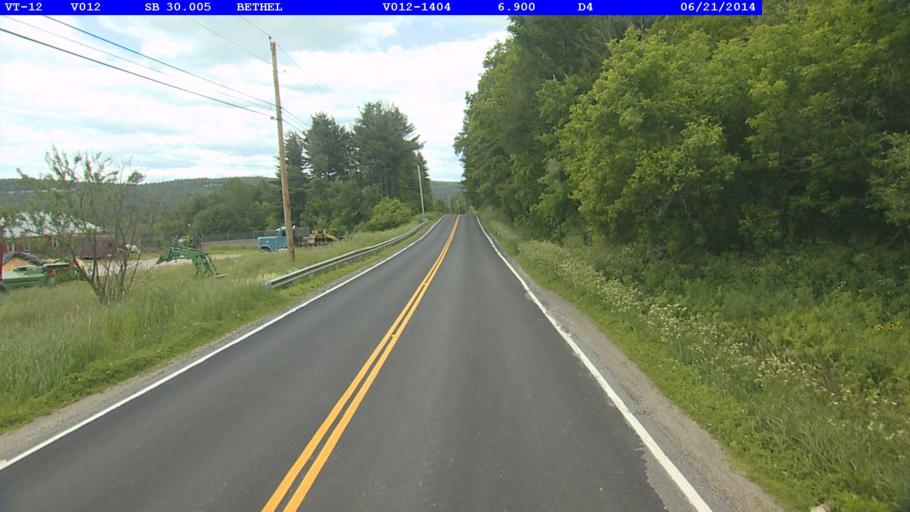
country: US
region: Vermont
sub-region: Orange County
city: Randolph
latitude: 43.8936
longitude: -72.6511
